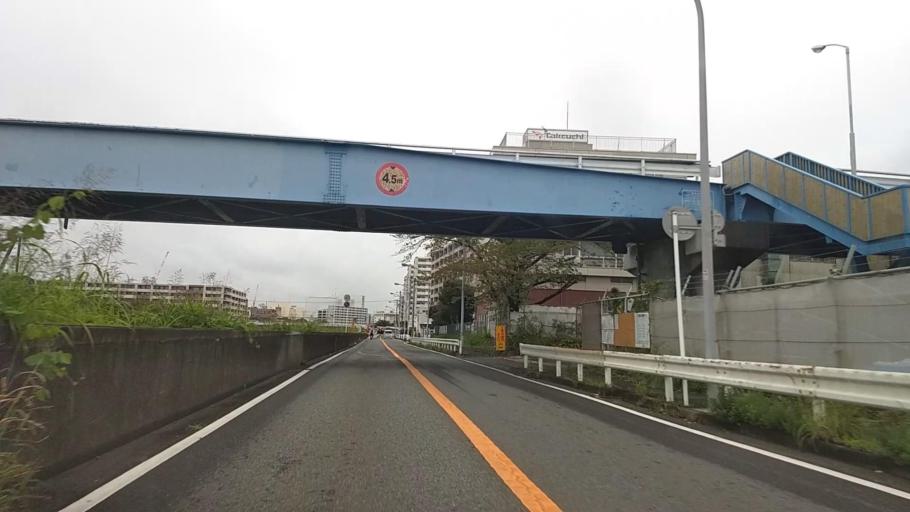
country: JP
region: Kanagawa
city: Fujisawa
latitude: 35.3926
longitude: 139.5333
